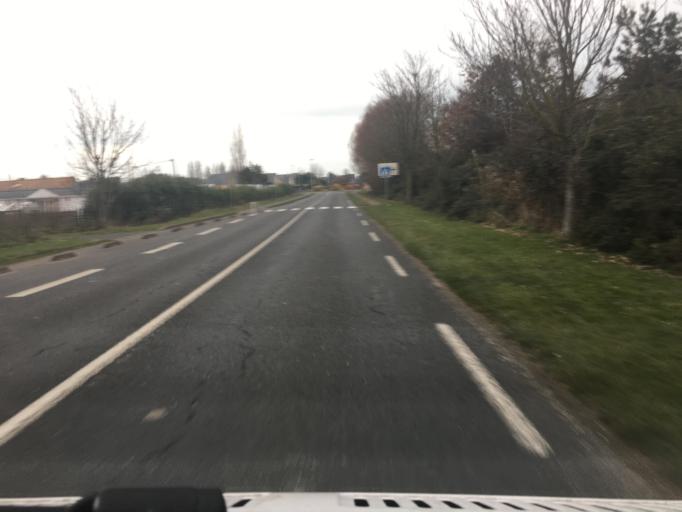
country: FR
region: Lower Normandy
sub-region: Departement du Calvados
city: Cabourg
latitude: 49.2817
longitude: -0.1356
